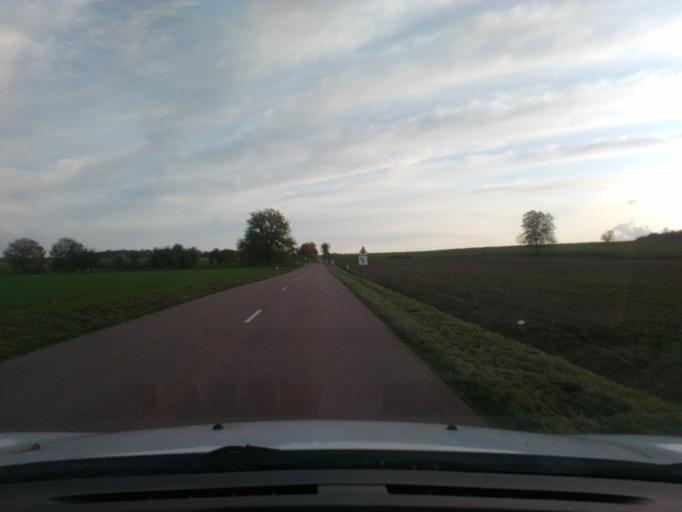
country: FR
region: Lorraine
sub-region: Departement des Vosges
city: Mirecourt
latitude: 48.2269
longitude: 6.1494
